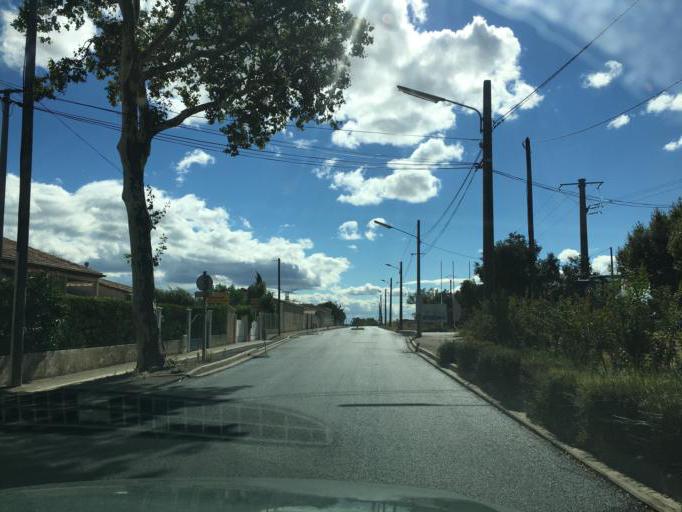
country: FR
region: Languedoc-Roussillon
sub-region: Departement de l'Herault
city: Pomerols
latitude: 43.3904
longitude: 3.4924
